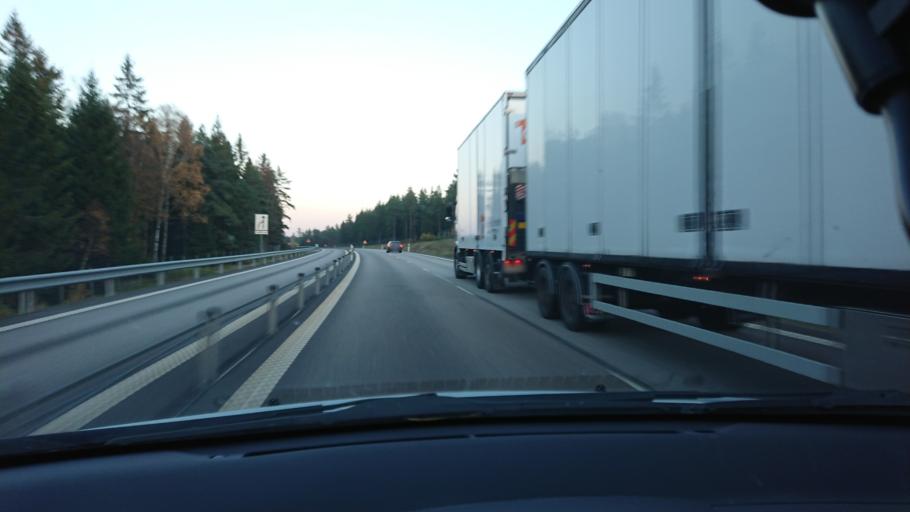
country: SE
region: Halland
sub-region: Laholms Kommun
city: Knared
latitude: 56.7248
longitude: 13.3759
